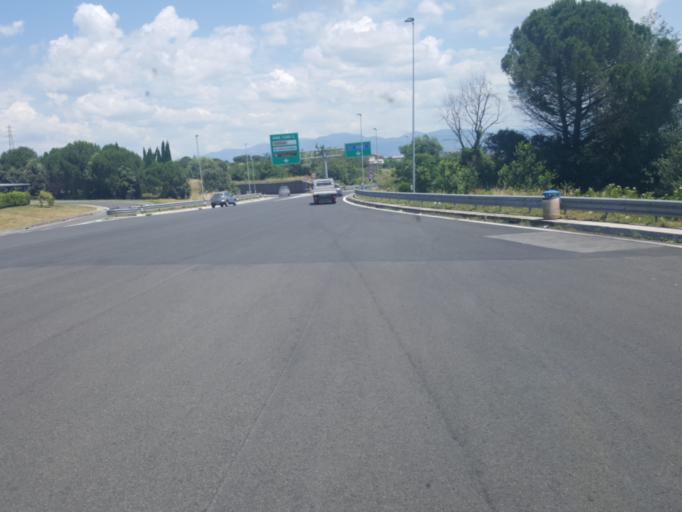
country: IT
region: Latium
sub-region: Citta metropolitana di Roma Capitale
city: Fiano Romano
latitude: 42.1398
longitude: 12.6073
